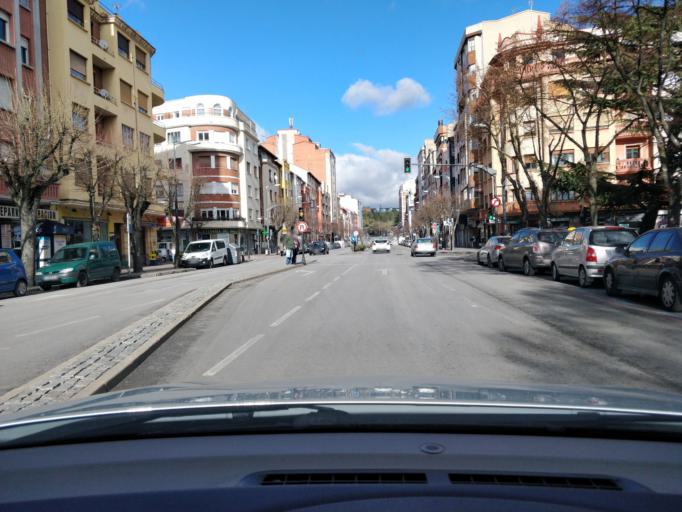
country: ES
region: Castille and Leon
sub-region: Provincia de Burgos
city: Burgos
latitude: 42.3477
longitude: -3.6970
